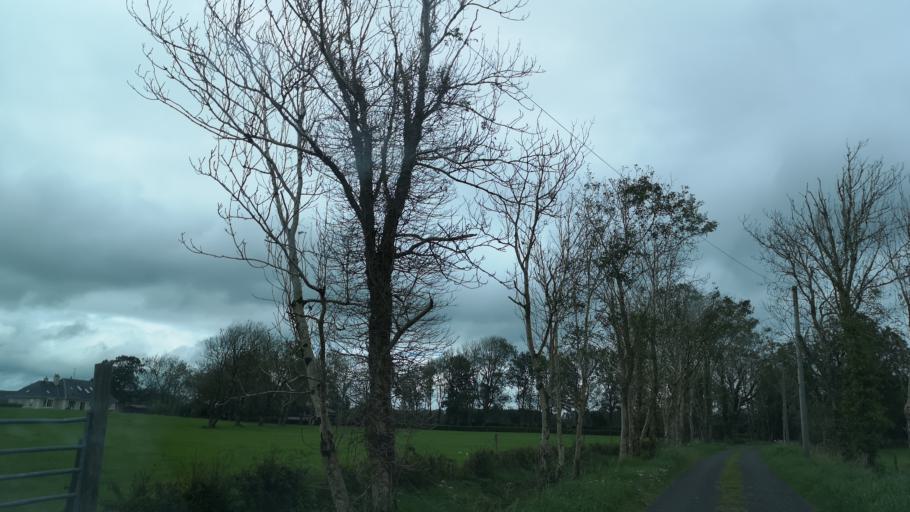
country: IE
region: Connaught
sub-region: County Galway
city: Athenry
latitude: 53.2987
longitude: -8.6675
